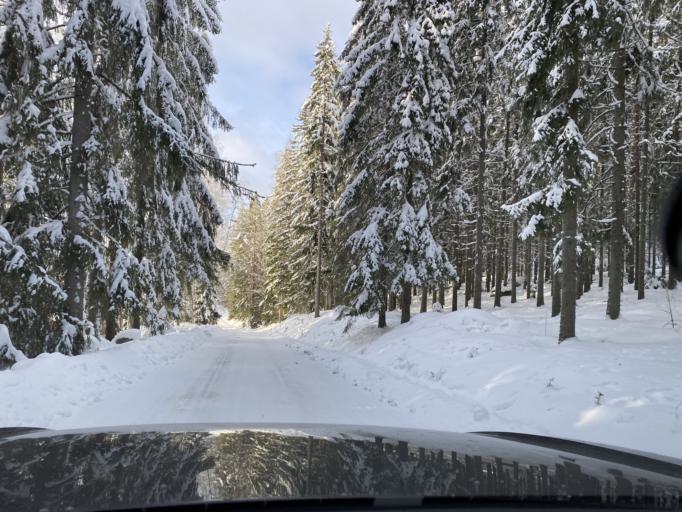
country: FI
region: Pirkanmaa
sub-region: Lounais-Pirkanmaa
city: Punkalaidun
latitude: 61.0738
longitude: 23.2299
